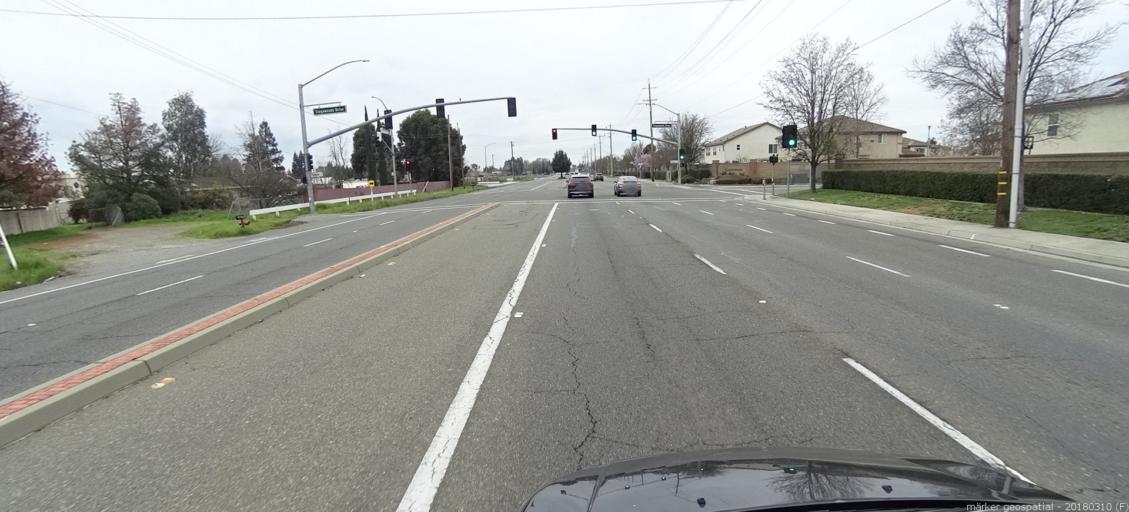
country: US
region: California
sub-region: Sacramento County
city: Vineyard
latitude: 38.4778
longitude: -121.3719
